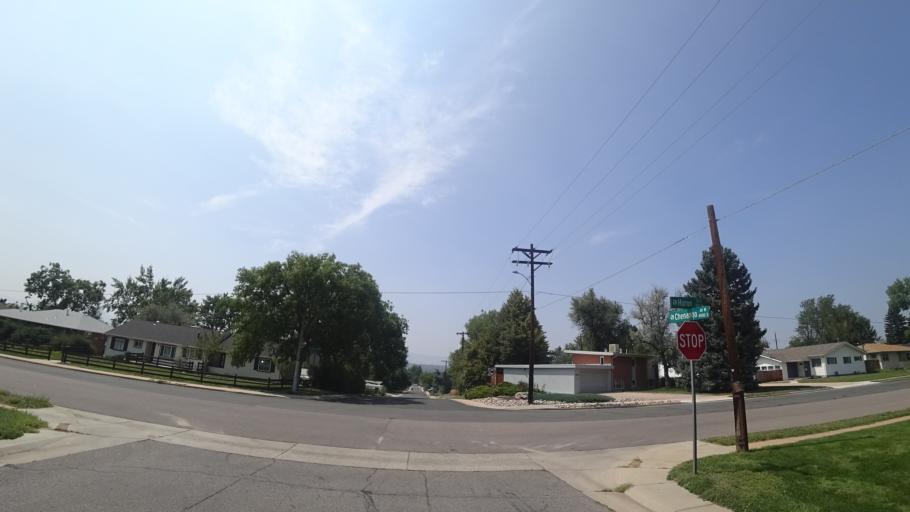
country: US
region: Colorado
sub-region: Arapahoe County
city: Englewood
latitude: 39.6277
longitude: -104.9972
